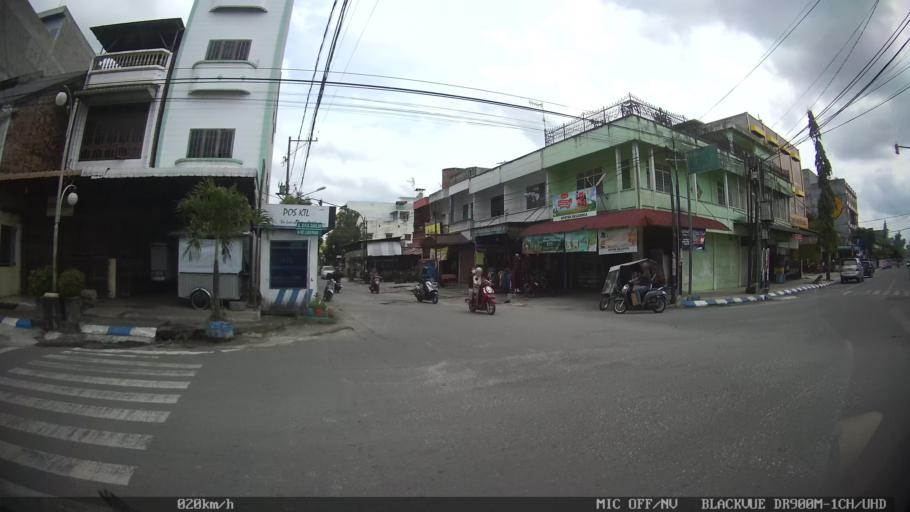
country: ID
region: North Sumatra
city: Percut
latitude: 3.5608
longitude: 98.8737
